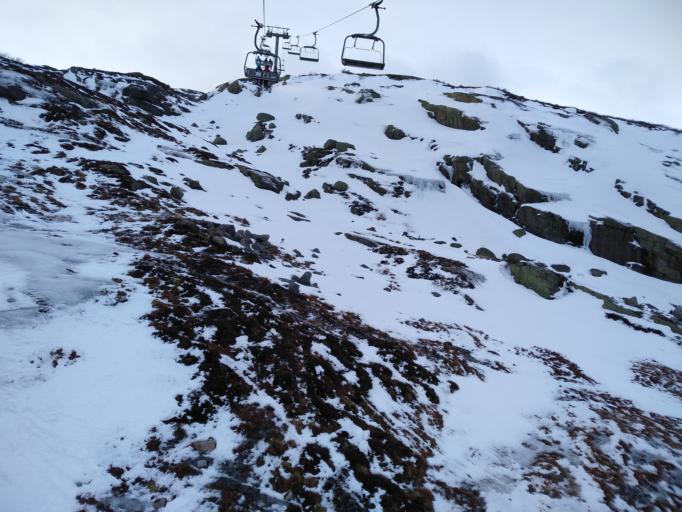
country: NO
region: Vest-Agder
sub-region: Sirdal
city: Tonstad
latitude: 58.9126
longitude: 6.8247
